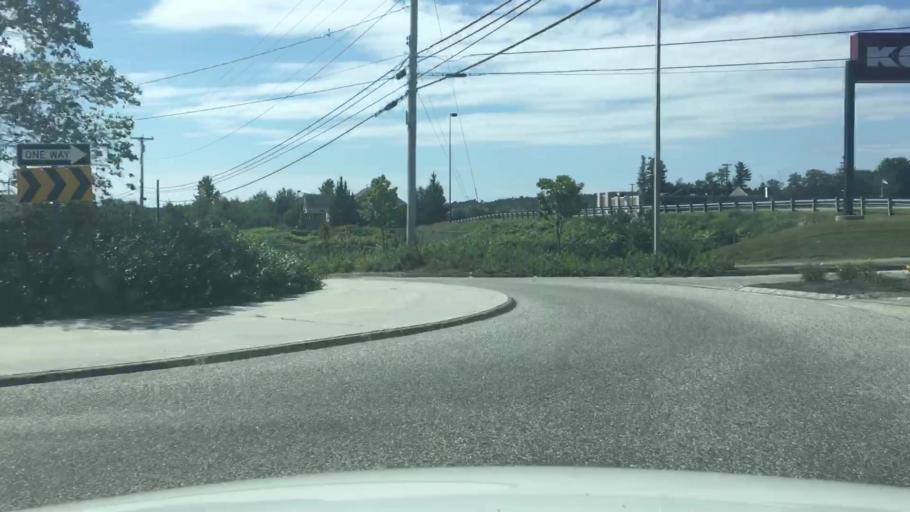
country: US
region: Maine
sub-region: Androscoggin County
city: Auburn
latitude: 44.1219
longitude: -70.2332
